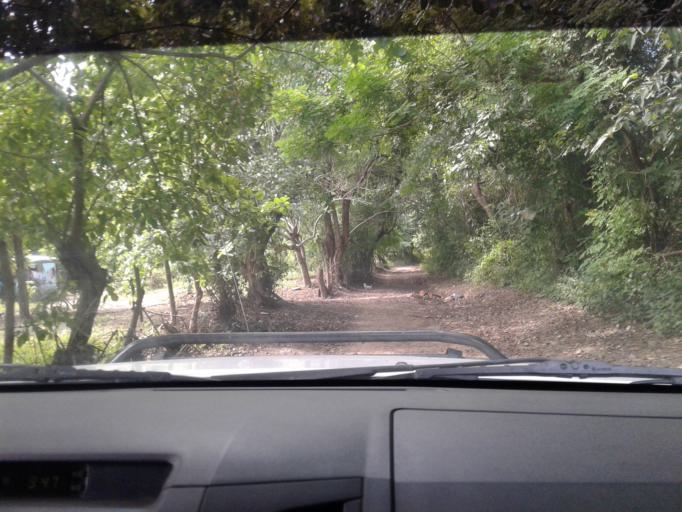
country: NI
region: Rivas
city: Tola
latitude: 11.4384
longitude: -85.9244
